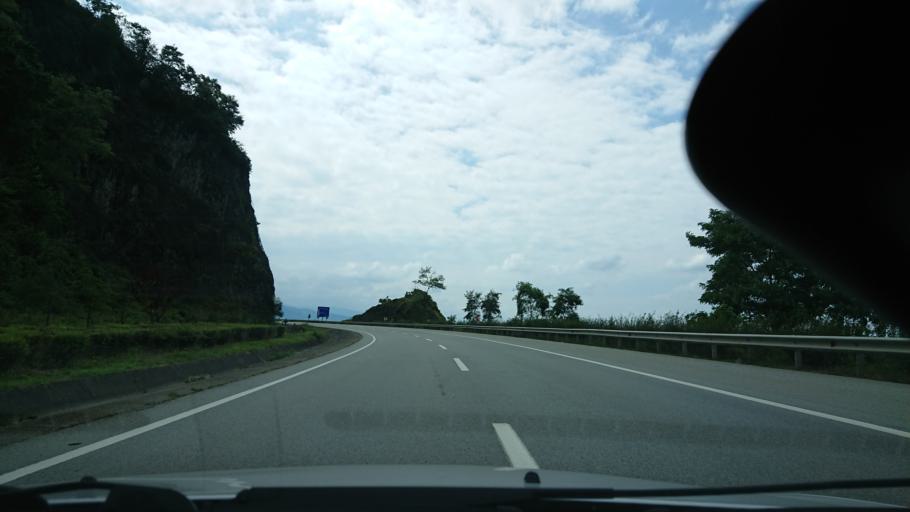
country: TR
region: Giresun
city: Kesap
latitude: 40.9432
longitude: 38.5818
